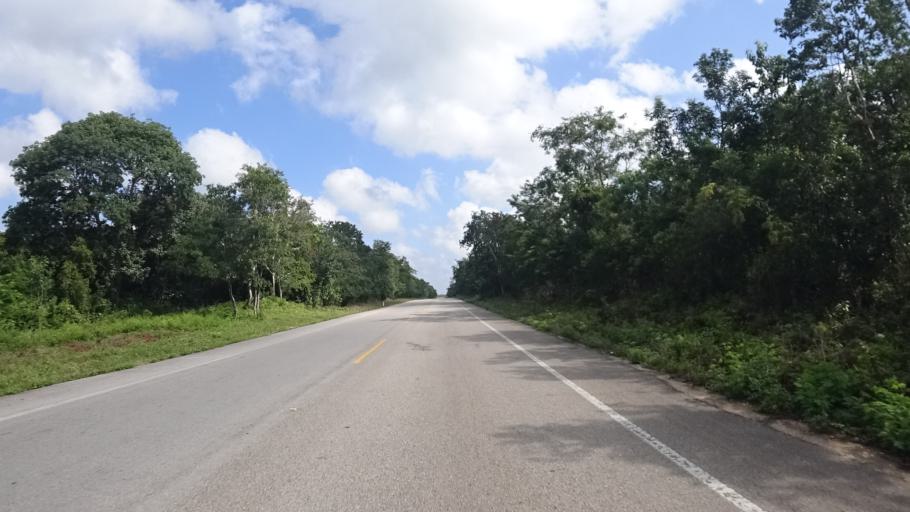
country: MX
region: Yucatan
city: Espita
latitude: 20.9852
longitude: -88.1766
